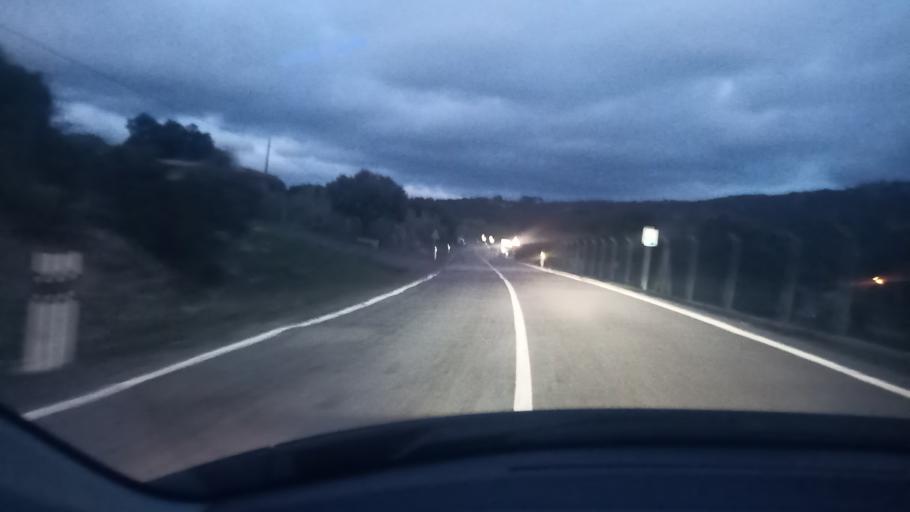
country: ES
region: Madrid
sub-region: Provincia de Madrid
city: Navas del Rey
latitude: 40.4316
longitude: -4.2486
